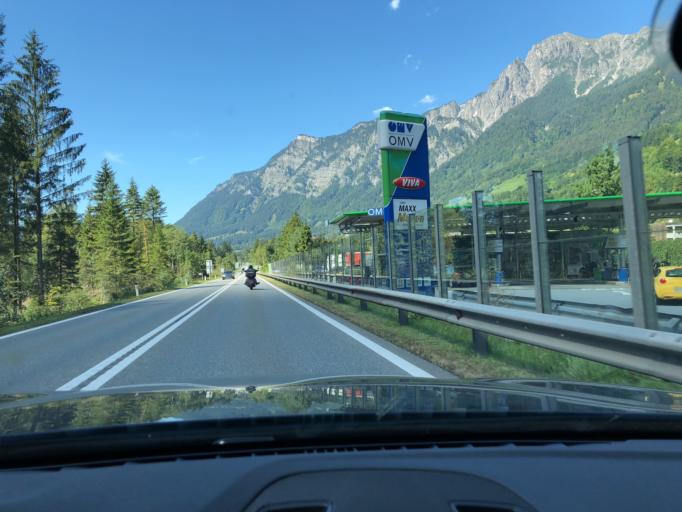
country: AT
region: Vorarlberg
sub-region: Politischer Bezirk Bludenz
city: Innerbraz
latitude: 47.1403
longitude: 9.9259
